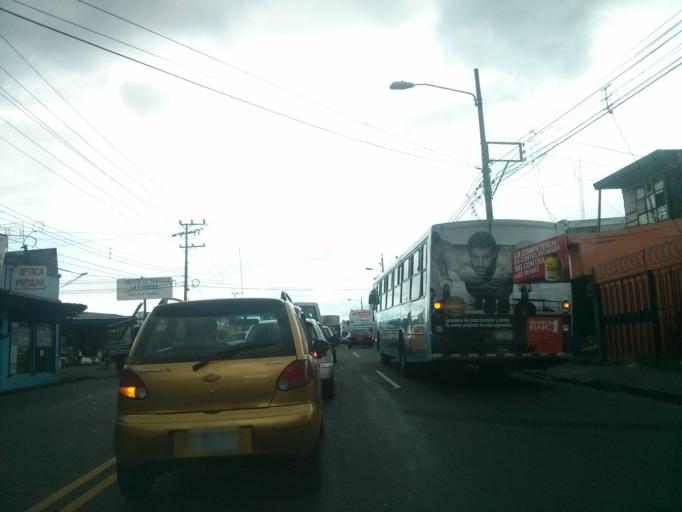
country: CR
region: San Jose
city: San Jose
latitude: 9.9165
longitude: -84.0698
